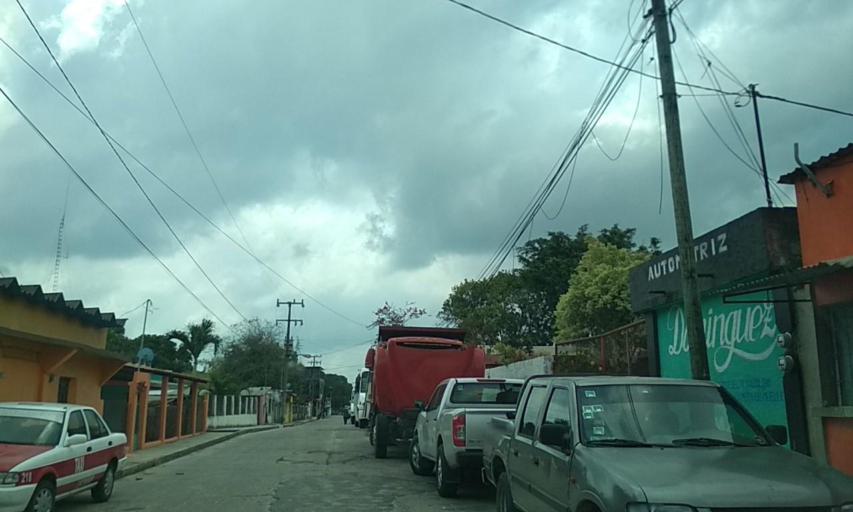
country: MX
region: Veracruz
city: Las Choapas
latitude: 17.8987
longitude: -94.1022
